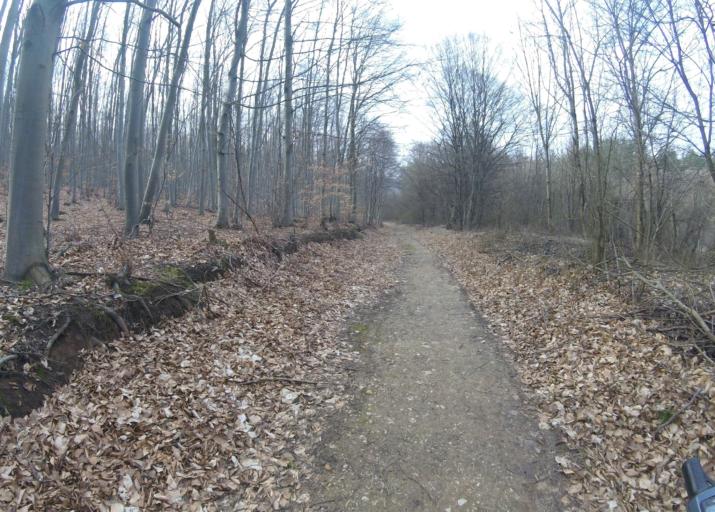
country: HU
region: Heves
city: Belapatfalva
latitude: 48.0448
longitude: 20.3619
